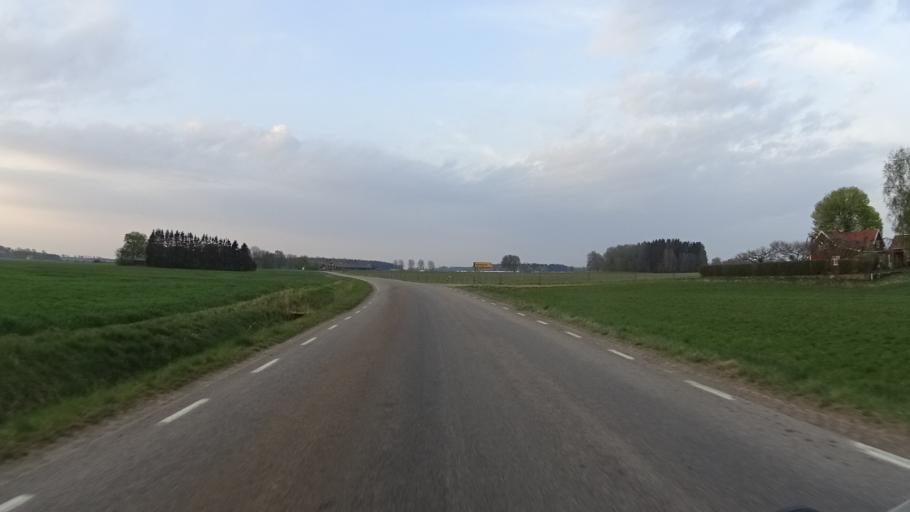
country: SE
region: Vaestra Goetaland
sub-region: Gotene Kommun
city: Kallby
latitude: 58.4704
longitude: 13.3295
